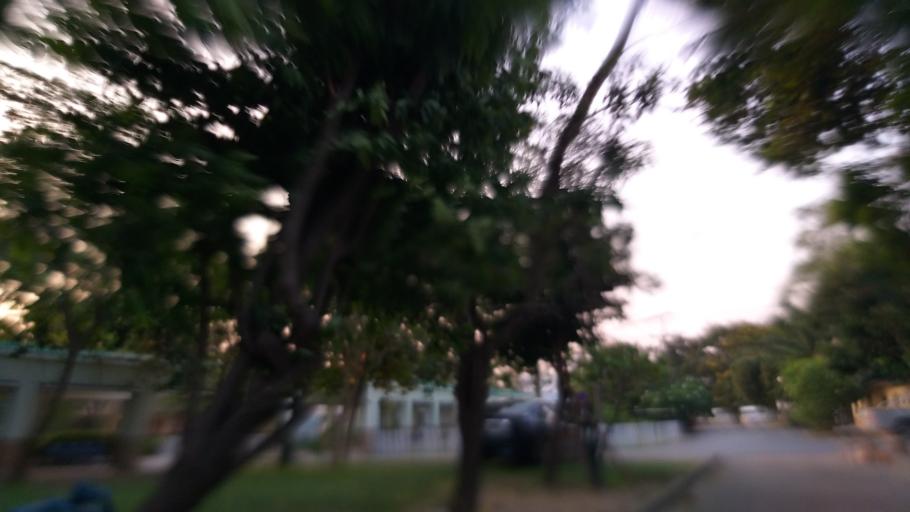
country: TH
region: Pathum Thani
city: Nong Suea
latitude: 14.0689
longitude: 100.8371
